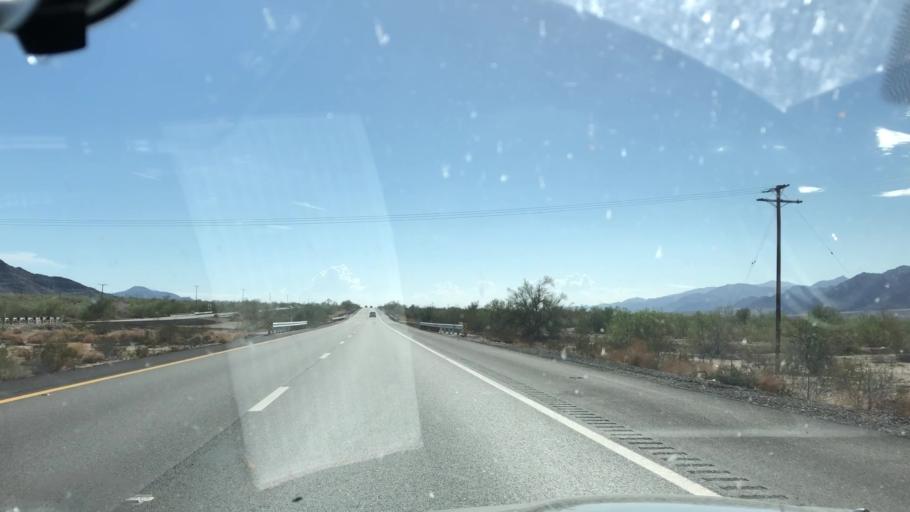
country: US
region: California
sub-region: Imperial County
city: Niland
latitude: 33.7001
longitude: -115.4648
